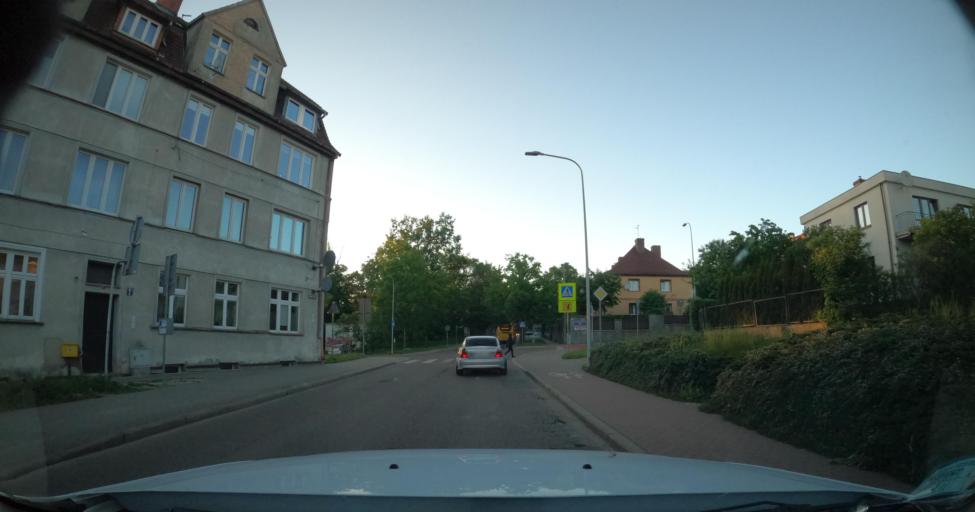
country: PL
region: Pomeranian Voivodeship
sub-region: Slupsk
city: Slupsk
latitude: 54.4665
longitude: 17.0460
